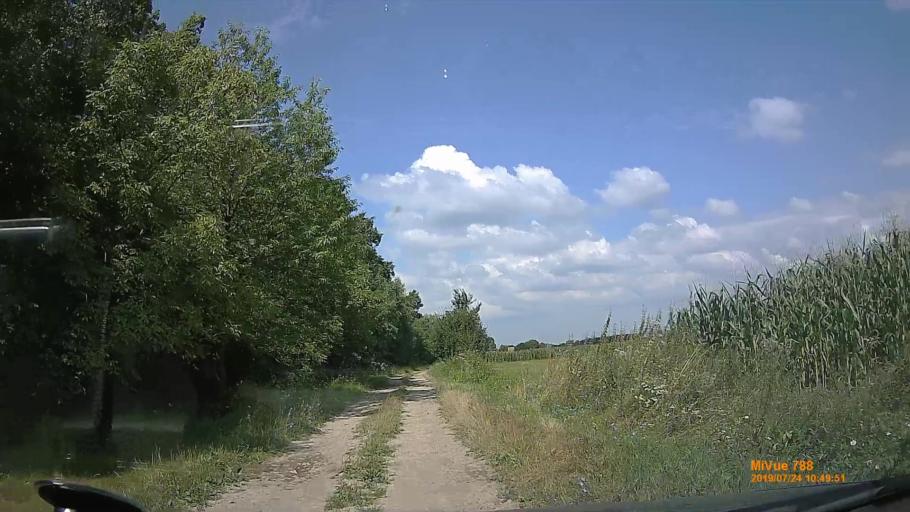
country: UA
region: Zakarpattia
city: Berehove
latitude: 48.1955
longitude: 22.5619
